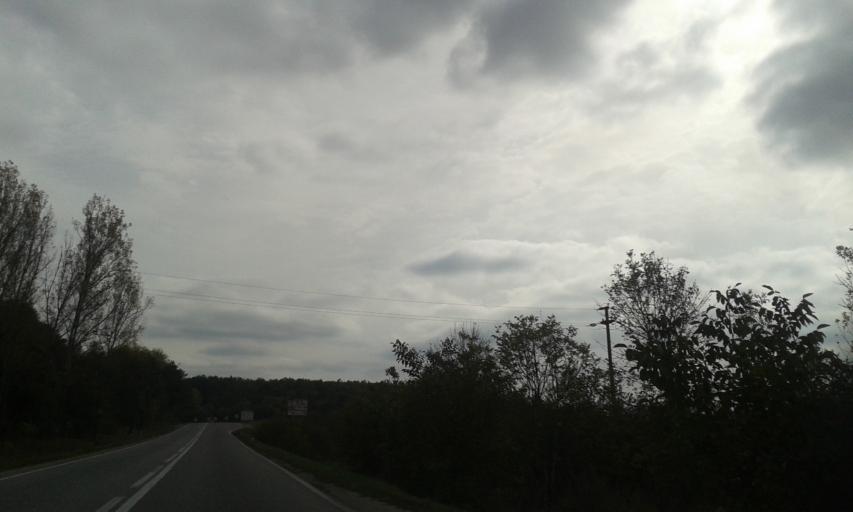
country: RO
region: Gorj
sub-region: Comuna Balanesti
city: Balanesti
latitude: 45.0351
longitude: 23.3744
